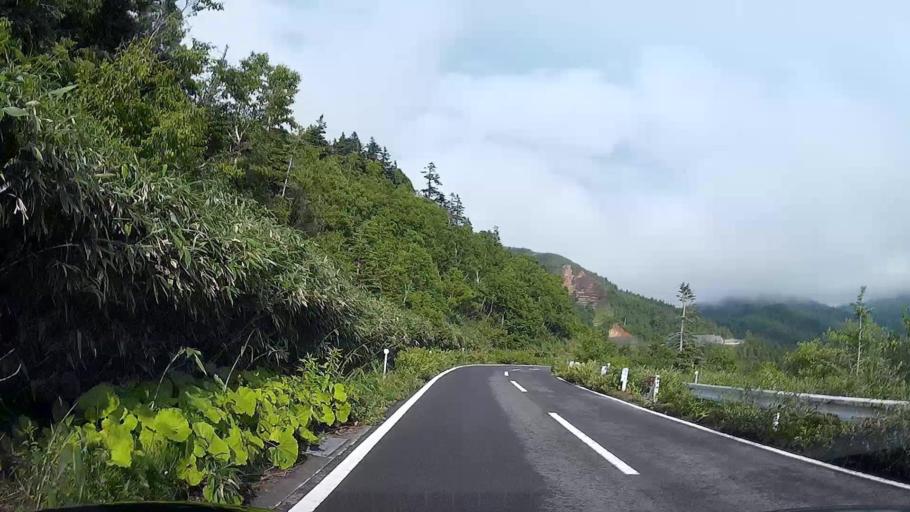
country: JP
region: Nagano
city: Nakano
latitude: 36.6416
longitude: 138.5209
